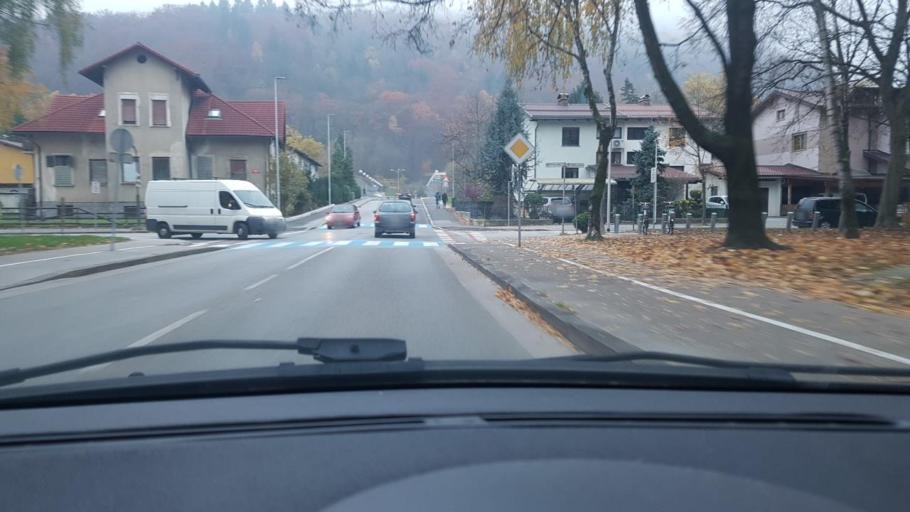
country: SI
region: Celje
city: Celje
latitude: 46.2332
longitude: 15.2529
